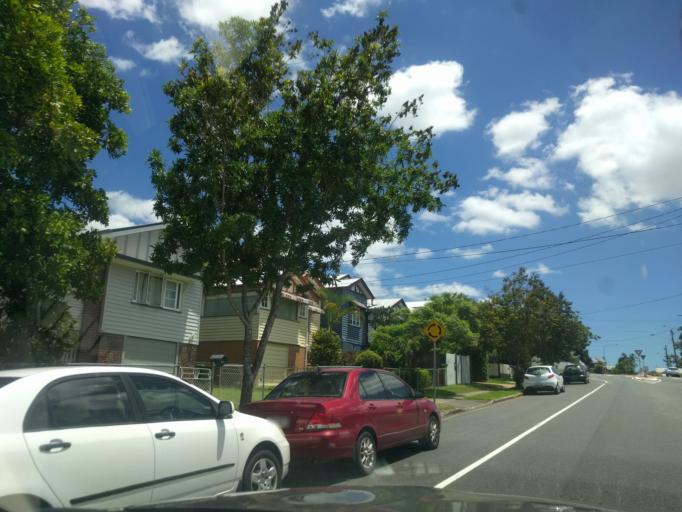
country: AU
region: Queensland
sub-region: Brisbane
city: Gordon Park
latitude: -27.4135
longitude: 153.0271
